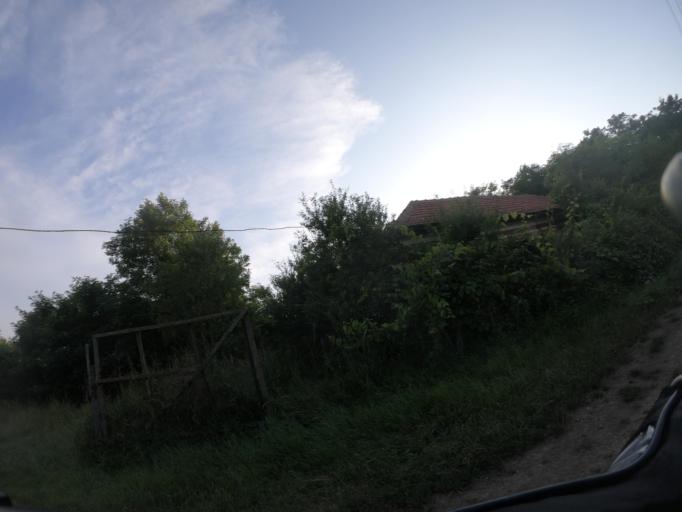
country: HU
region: Borsod-Abauj-Zemplen
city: Mezokeresztes
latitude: 47.7691
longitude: 20.7865
